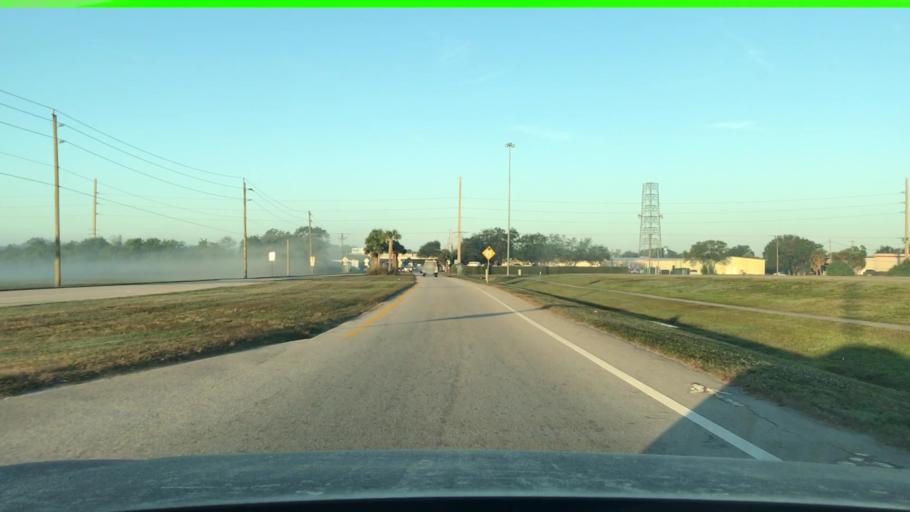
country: US
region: Florida
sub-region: Sarasota County
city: Fruitville
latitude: 27.3259
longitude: -82.4438
